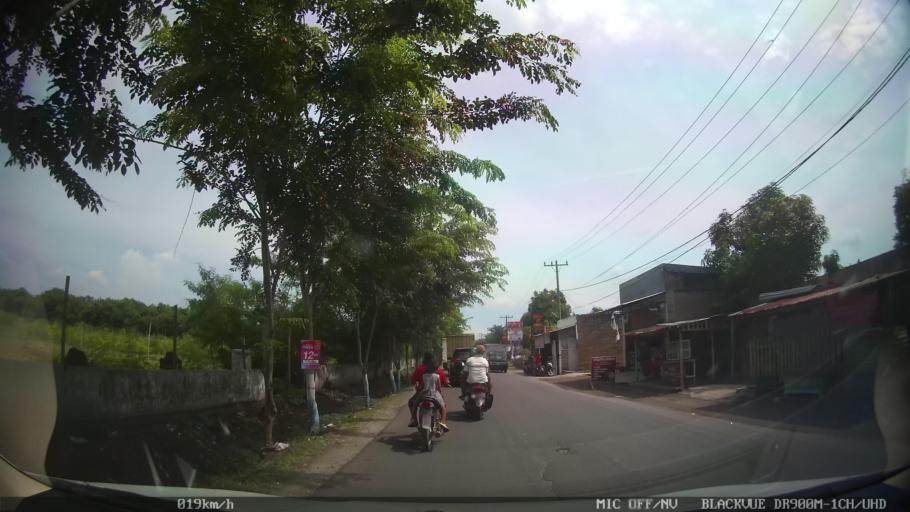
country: ID
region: North Sumatra
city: Medan
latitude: 3.6296
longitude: 98.7159
